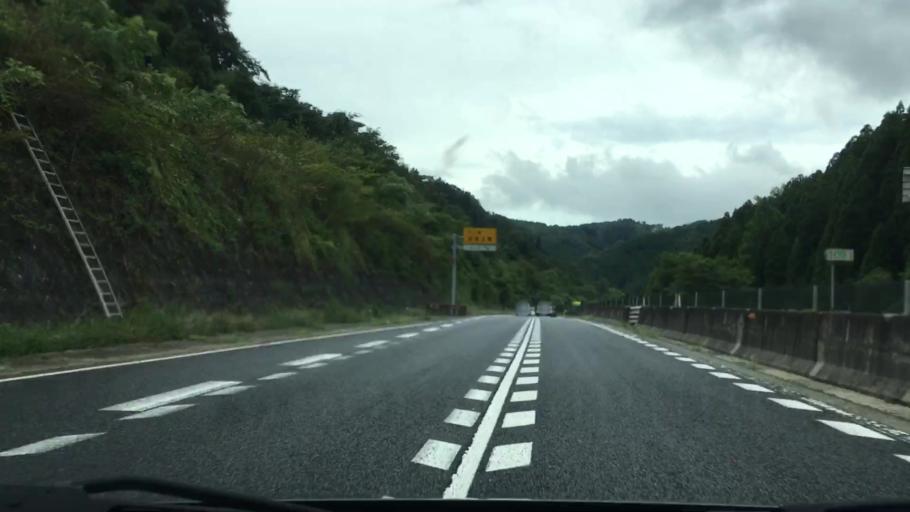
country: JP
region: Hyogo
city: Yamazakicho-nakabirose
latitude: 35.0434
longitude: 134.4657
